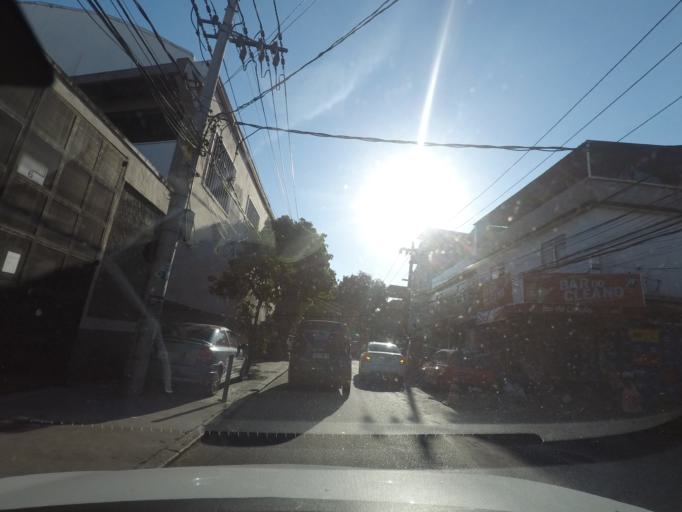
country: BR
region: Rio de Janeiro
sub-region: Rio De Janeiro
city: Rio de Janeiro
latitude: -22.8895
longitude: -43.2285
